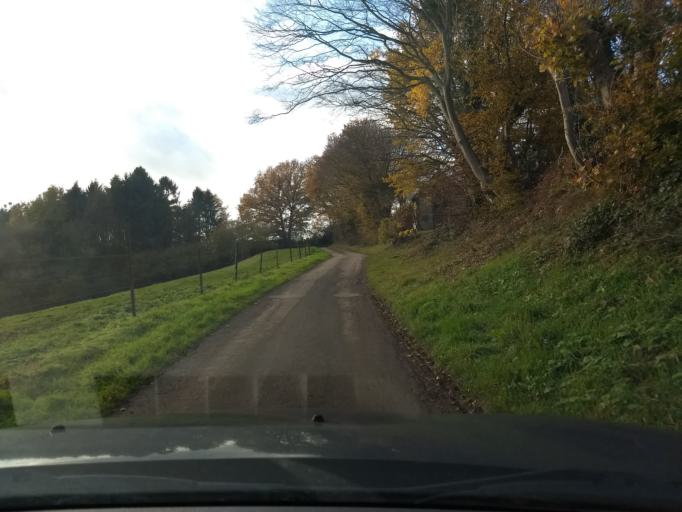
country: BE
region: Wallonia
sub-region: Province du Brabant Wallon
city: Ittre
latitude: 50.5983
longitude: 4.2782
